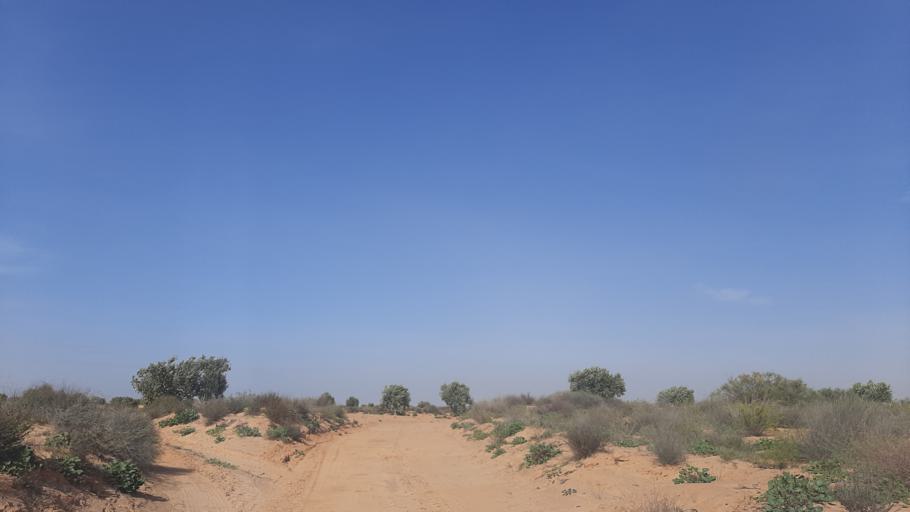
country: TN
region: Madanin
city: Zarzis
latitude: 33.4520
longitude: 10.8086
